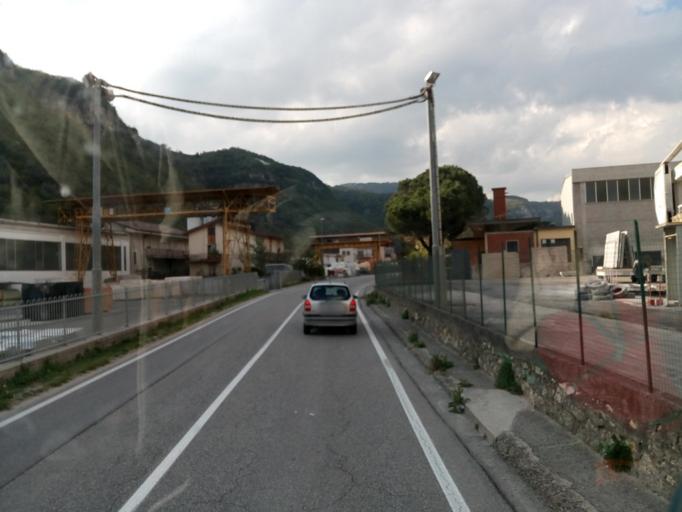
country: IT
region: Veneto
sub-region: Provincia di Verona
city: Stallavena-Lugo
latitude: 45.5602
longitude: 10.9979
